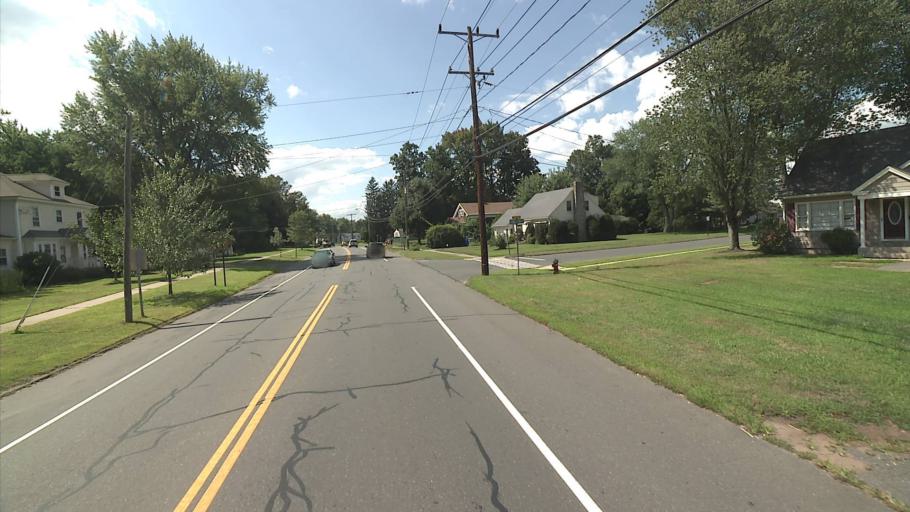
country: US
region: Connecticut
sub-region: Hartford County
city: Hazardville
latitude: 41.9854
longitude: -72.5245
